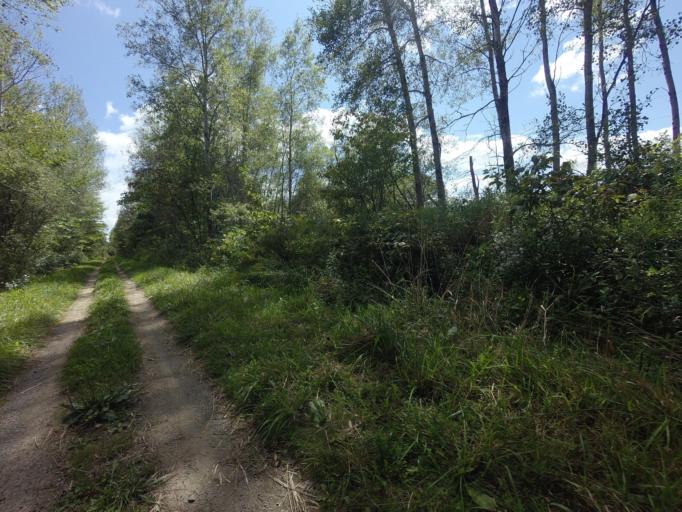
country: CA
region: Ontario
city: Orangeville
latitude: 43.7937
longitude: -80.2721
